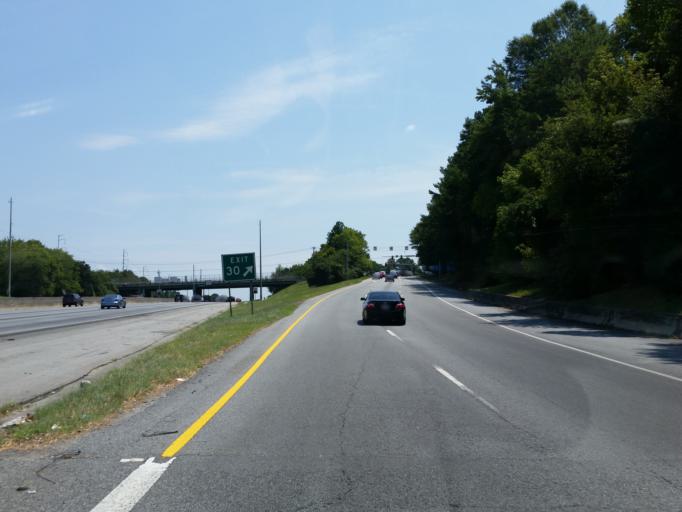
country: US
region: Georgia
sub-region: DeKalb County
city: Dunwoody
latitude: 33.9200
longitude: -84.3180
